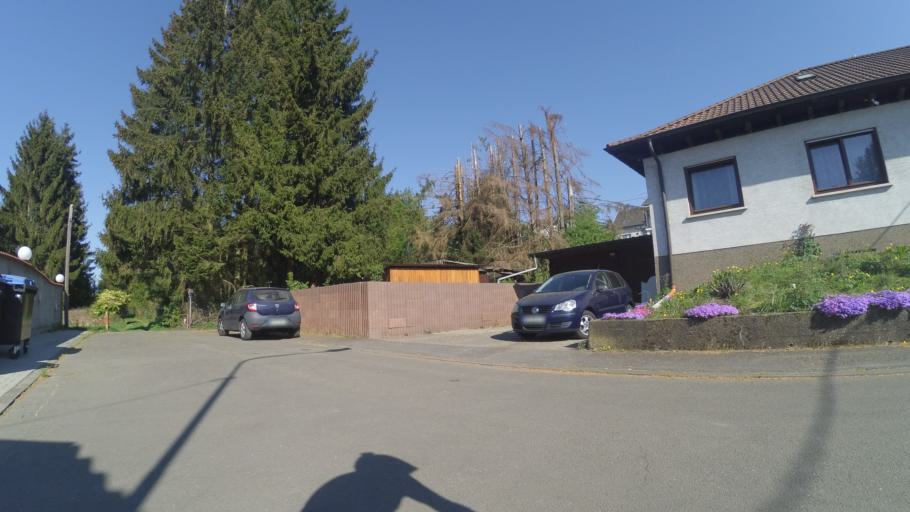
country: DE
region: Saarland
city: Hangard
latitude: 49.3717
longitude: 7.1925
